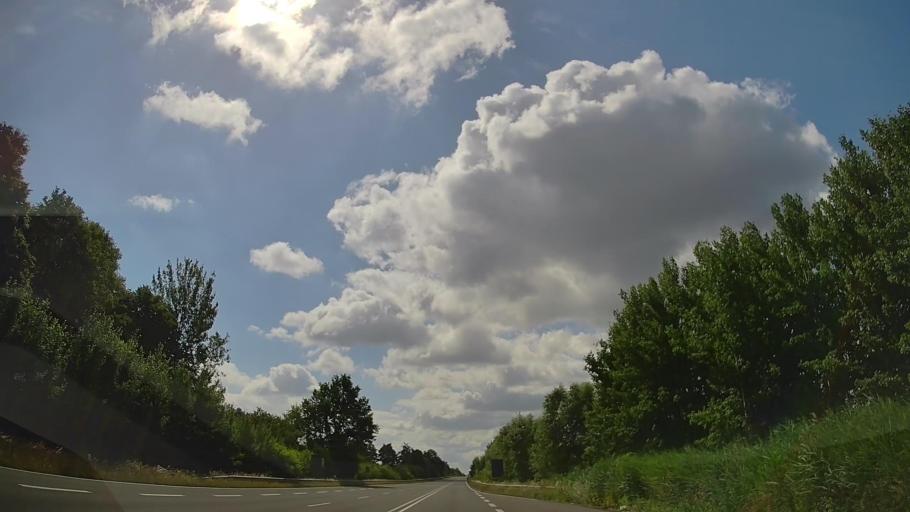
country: DE
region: Lower Saxony
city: Cappeln
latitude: 52.8402
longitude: 8.1096
